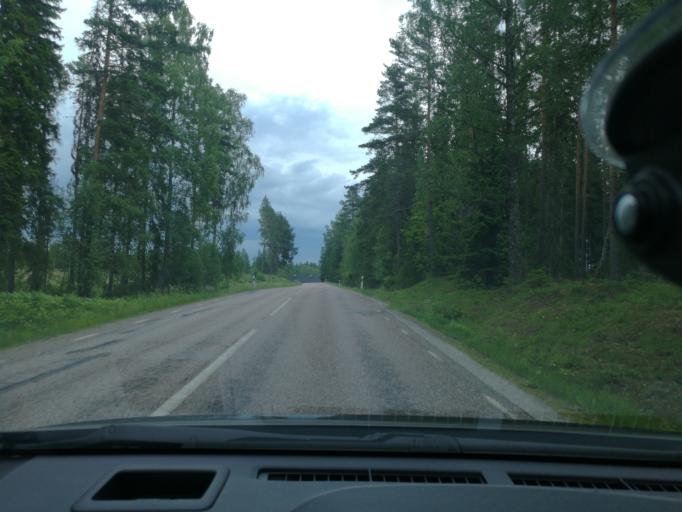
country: SE
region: Vaestmanland
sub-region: Vasteras
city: Skultuna
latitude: 59.9146
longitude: 16.3797
